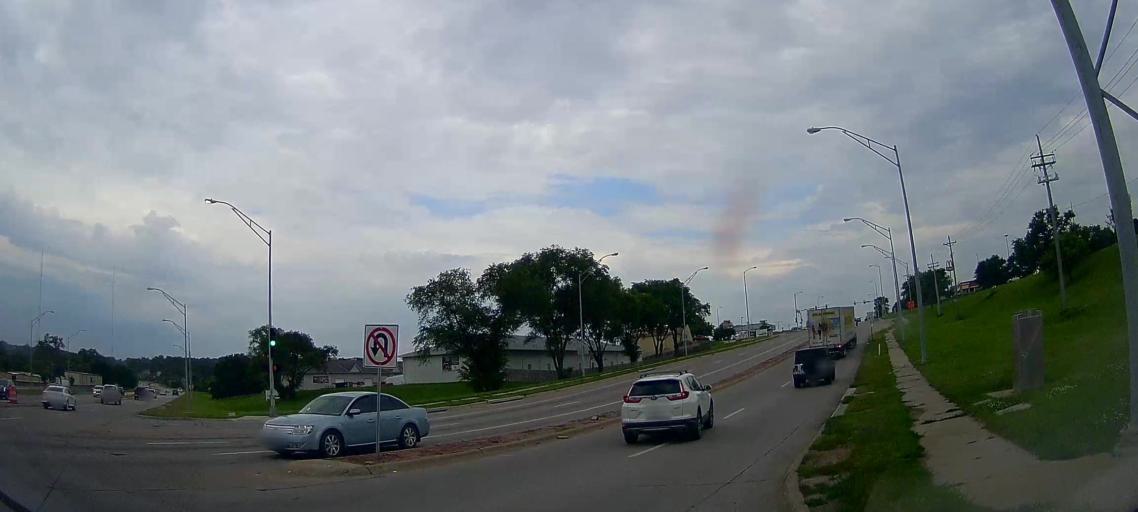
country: US
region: Nebraska
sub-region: Douglas County
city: Ralston
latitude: 41.3128
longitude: -96.0528
